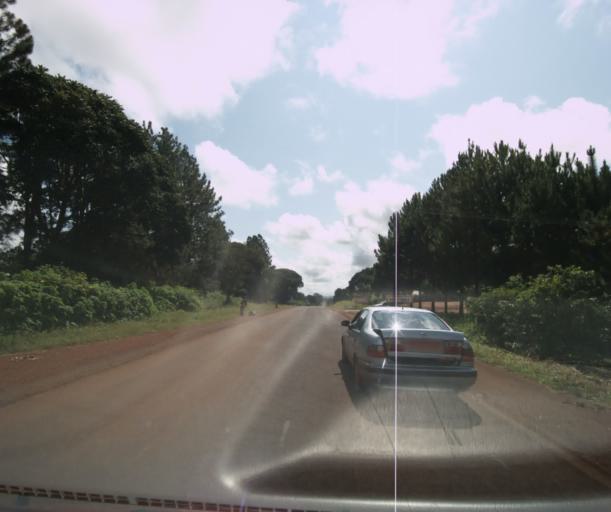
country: CM
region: West
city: Foumban
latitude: 5.6654
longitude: 10.7817
